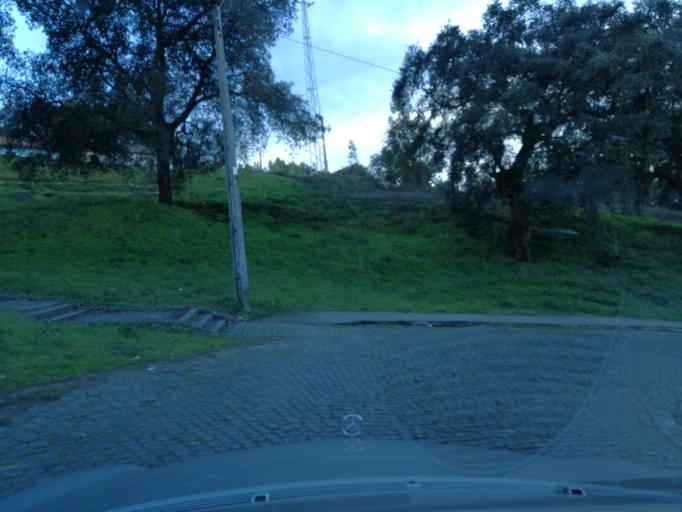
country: PT
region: Braga
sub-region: Braga
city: Braga
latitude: 41.5377
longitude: -8.4183
